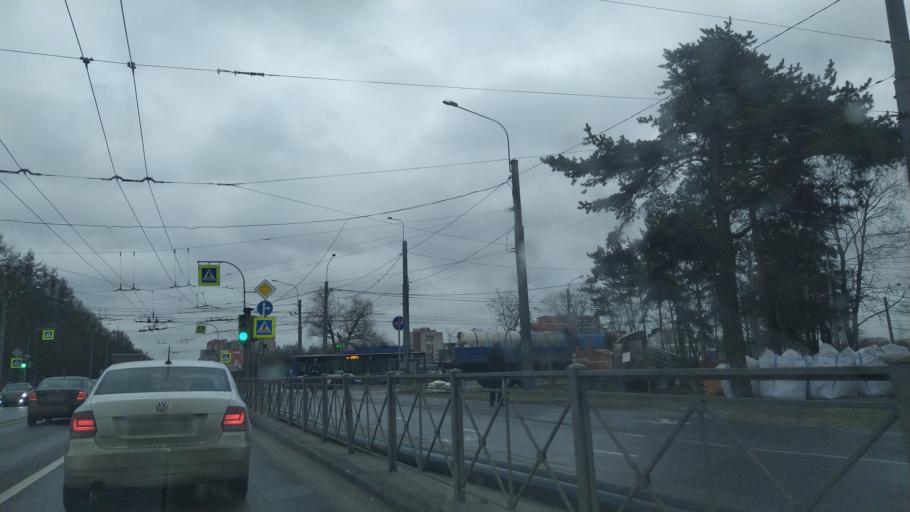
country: RU
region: St.-Petersburg
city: Sosnovka
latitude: 60.0129
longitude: 30.3530
